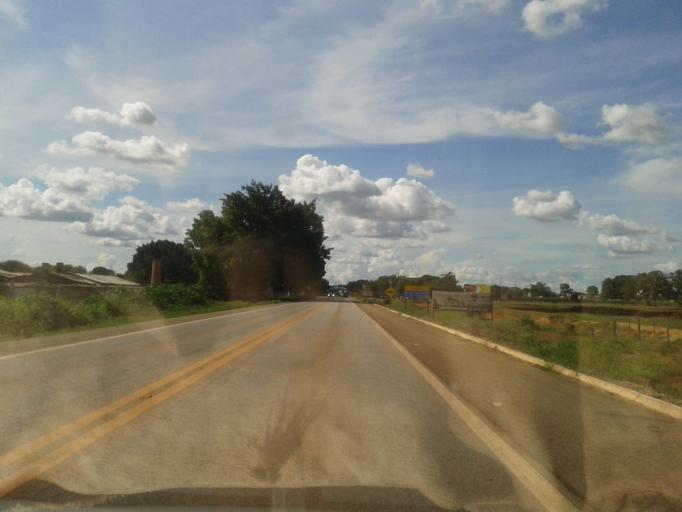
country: BR
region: Goias
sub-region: Mozarlandia
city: Mozarlandia
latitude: -15.1057
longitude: -50.6101
